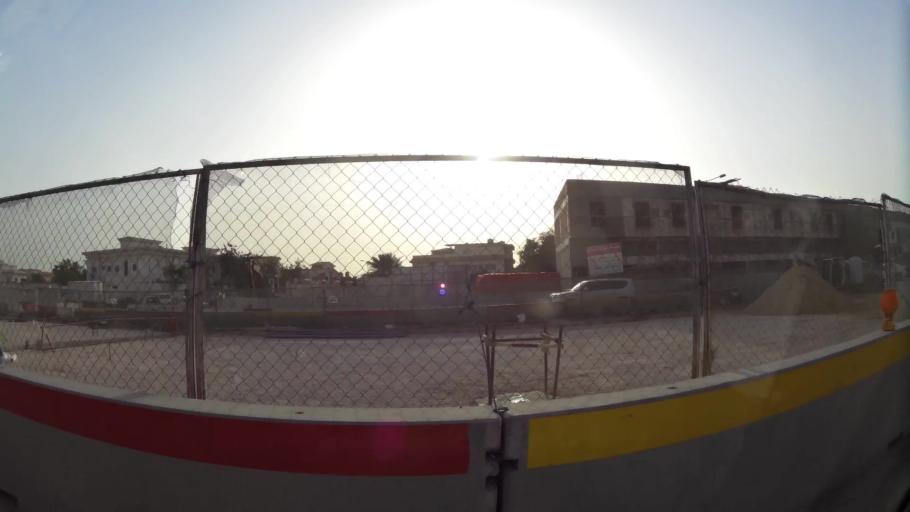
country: QA
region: Baladiyat ar Rayyan
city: Ar Rayyan
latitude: 25.2486
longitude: 51.4524
